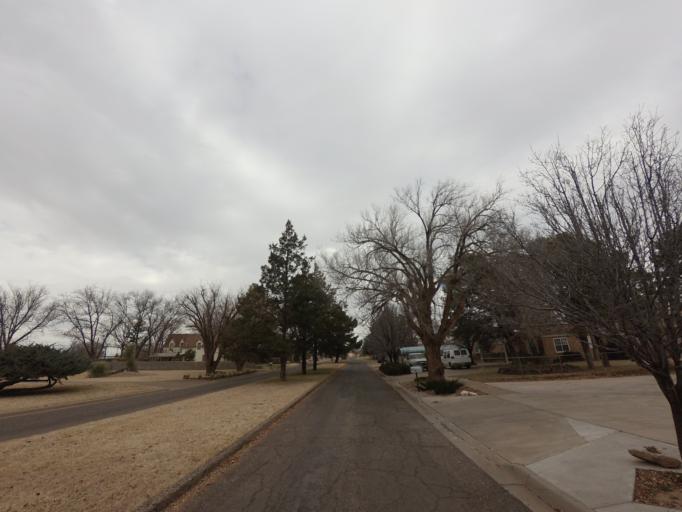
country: US
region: New Mexico
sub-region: Curry County
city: Clovis
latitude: 34.3793
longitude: -103.2007
